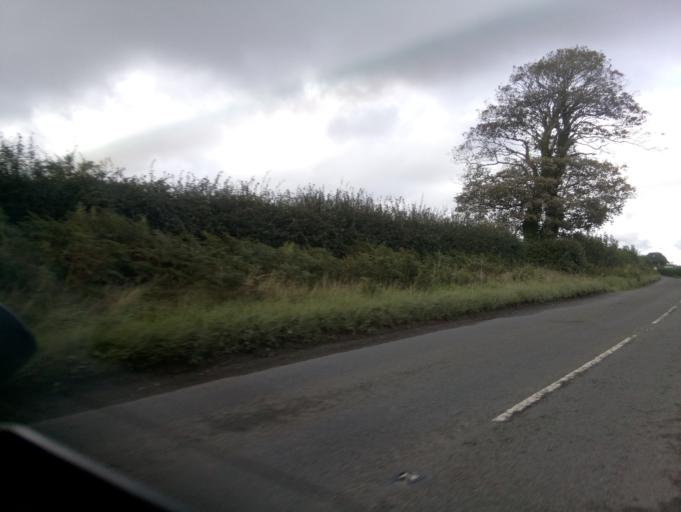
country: GB
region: England
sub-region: Devon
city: Kingsbridge
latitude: 50.2983
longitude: -3.7938
